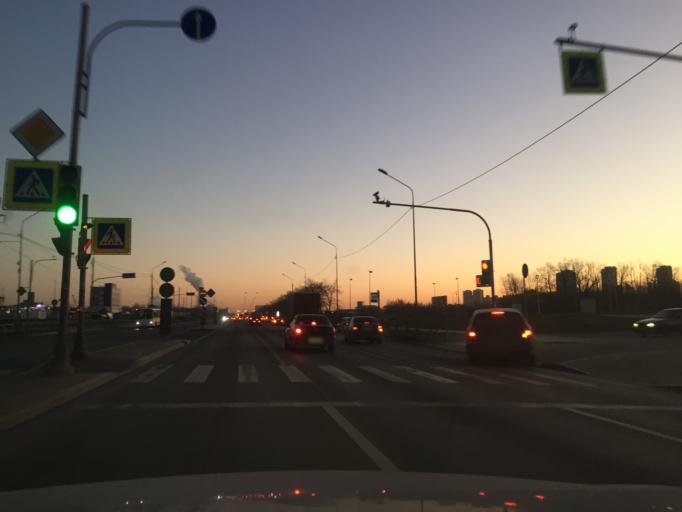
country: RU
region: St.-Petersburg
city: Obukhovo
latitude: 59.8589
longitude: 30.4208
